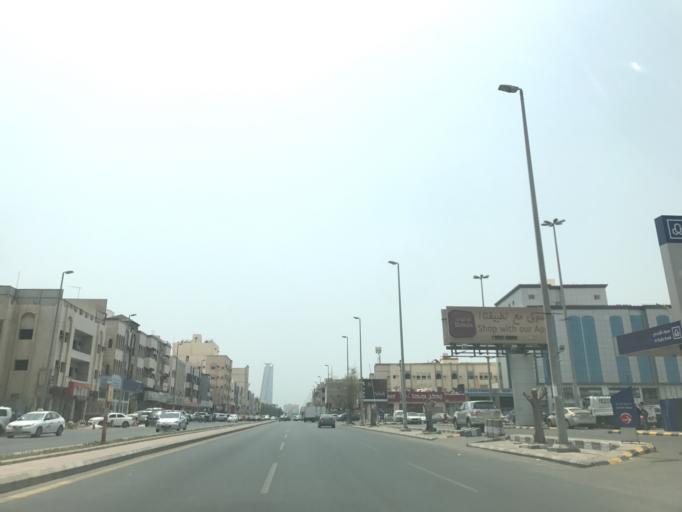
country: SA
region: Makkah
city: Jeddah
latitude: 21.6089
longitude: 39.1321
